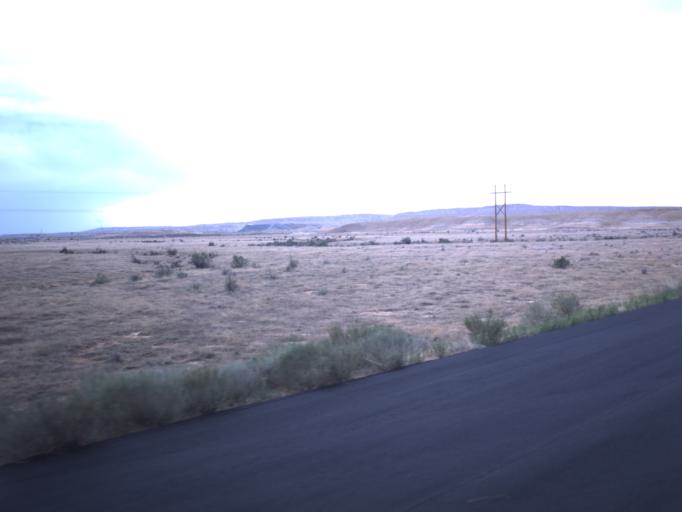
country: US
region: Utah
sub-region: Uintah County
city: Naples
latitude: 40.1140
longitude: -109.2402
